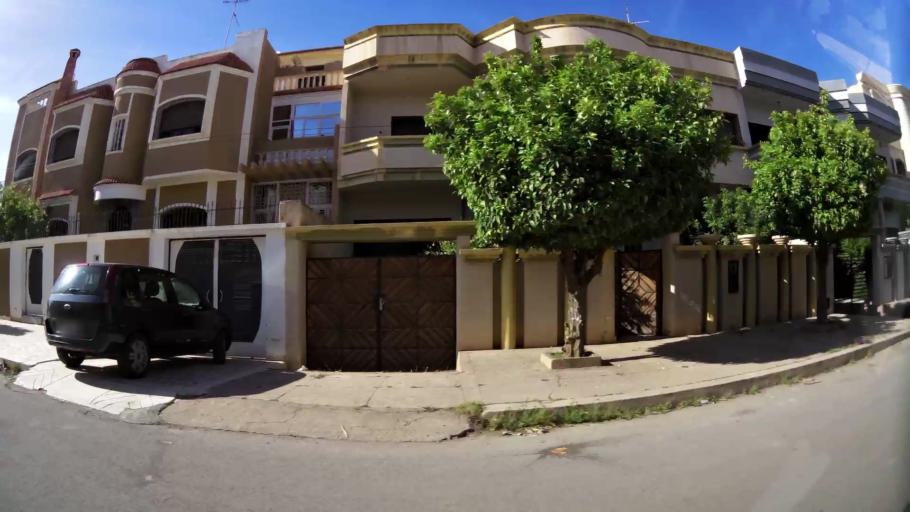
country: MA
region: Oriental
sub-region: Oujda-Angad
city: Oujda
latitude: 34.6664
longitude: -1.9051
